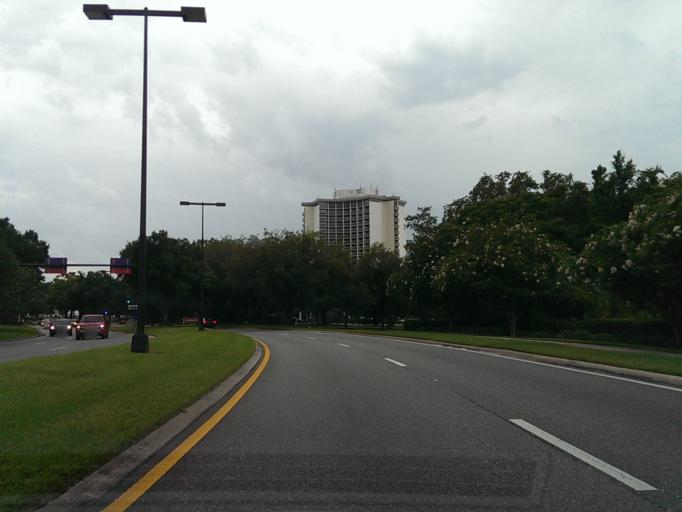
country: US
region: Florida
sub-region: Osceola County
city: Celebration
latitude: 28.3808
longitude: -81.5075
